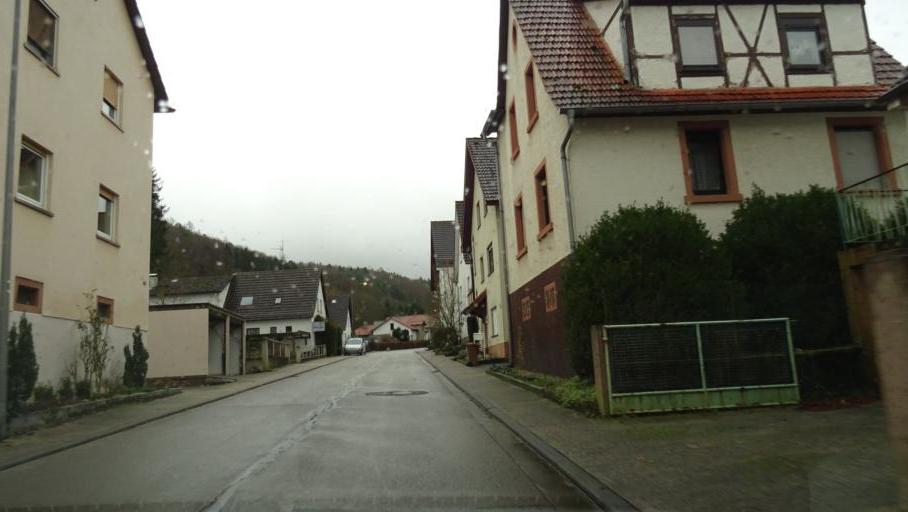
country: DE
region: Hesse
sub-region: Regierungsbezirk Darmstadt
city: Morlenbach
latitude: 49.5773
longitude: 8.7561
